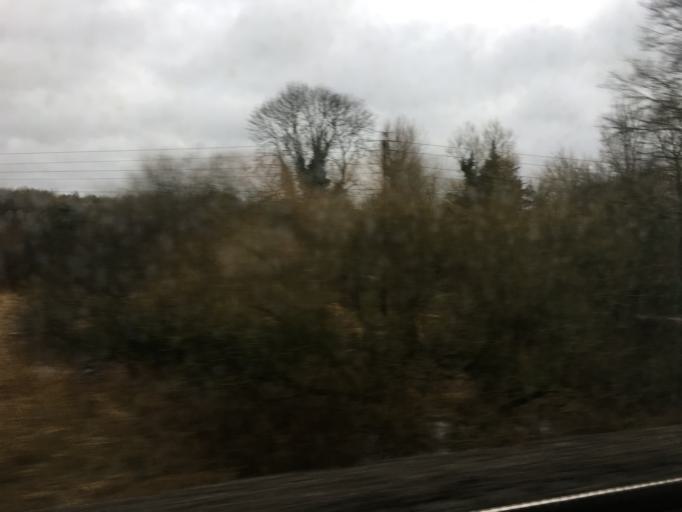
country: GB
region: England
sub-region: West Berkshire
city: Thatcham
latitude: 51.3965
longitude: -1.2756
